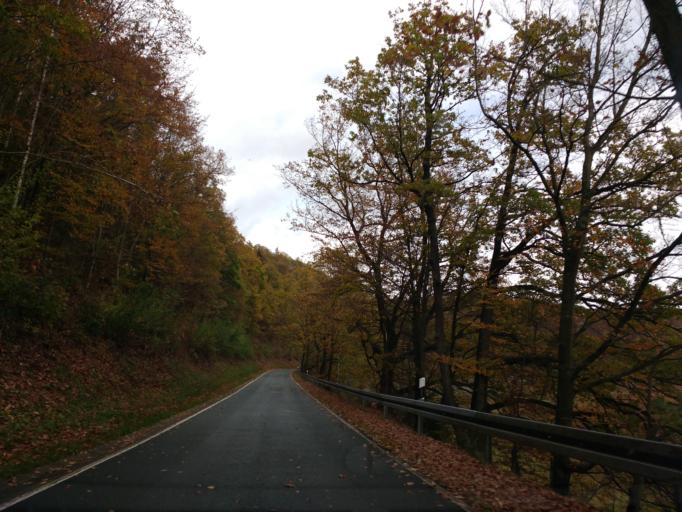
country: DE
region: Hesse
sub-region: Regierungsbezirk Kassel
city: Vohl
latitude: 51.1824
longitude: 8.9451
